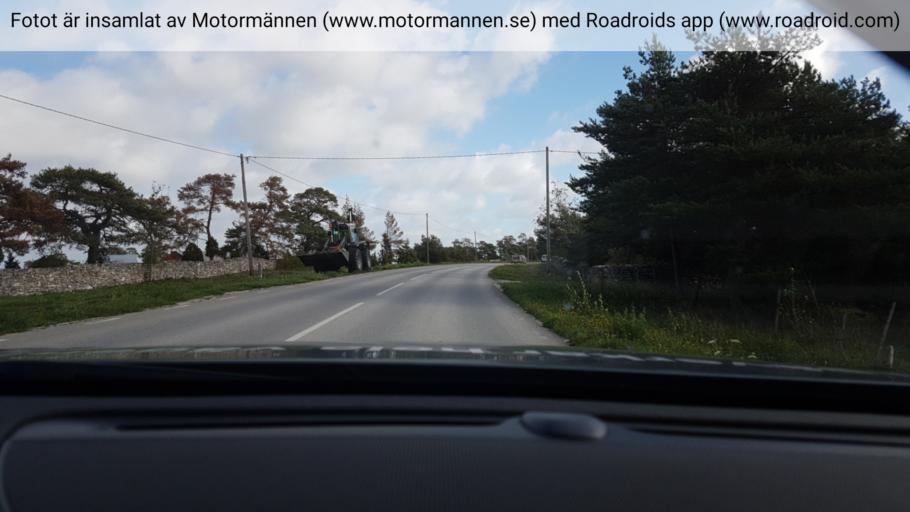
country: SE
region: Gotland
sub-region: Gotland
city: Slite
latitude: 57.9113
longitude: 19.1122
